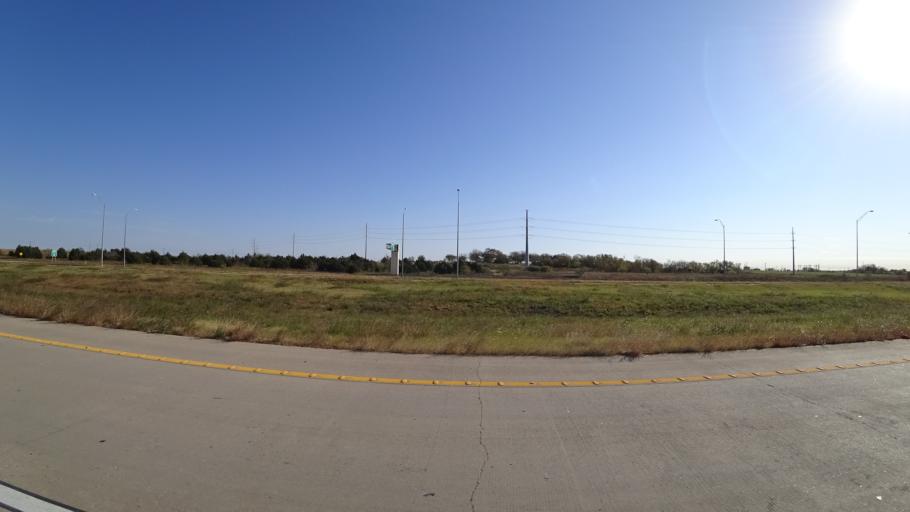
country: US
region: Texas
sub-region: Travis County
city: Pflugerville
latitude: 30.4171
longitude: -97.5866
